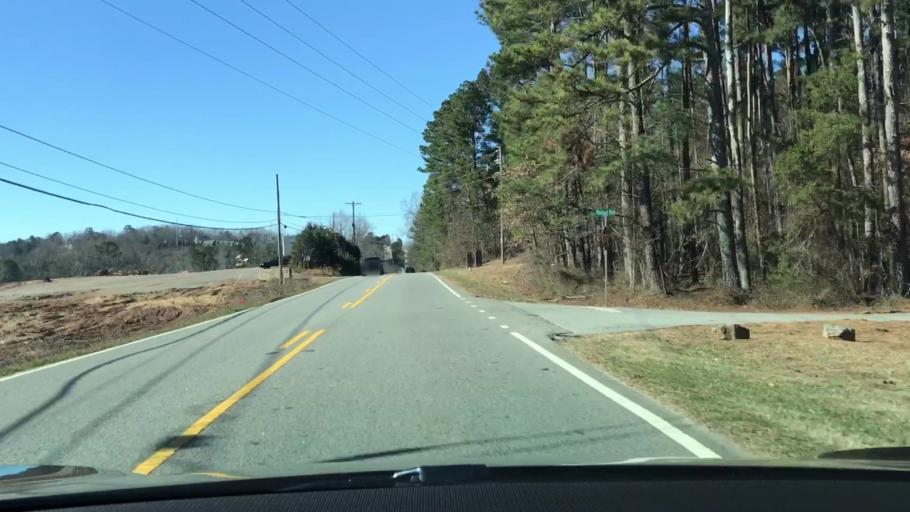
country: US
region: Georgia
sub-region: Forsyth County
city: Cumming
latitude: 34.1820
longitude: -84.0959
